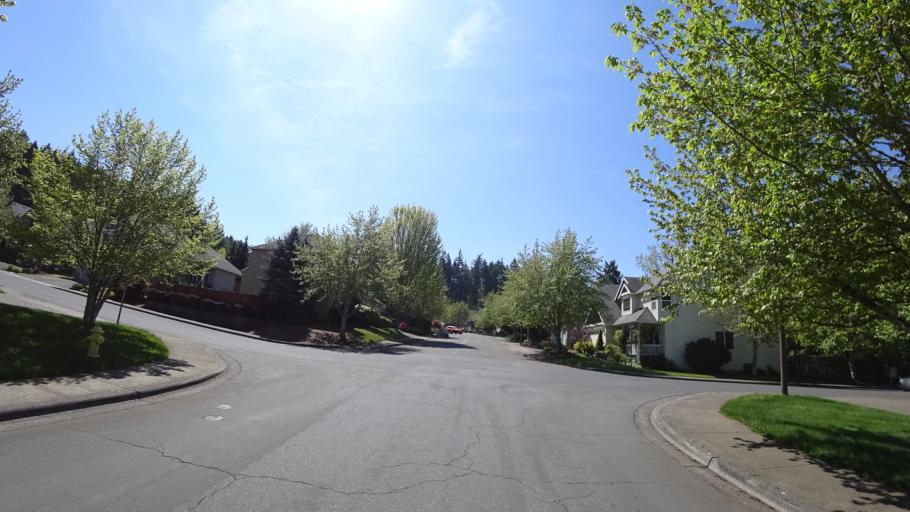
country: US
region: Oregon
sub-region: Washington County
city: King City
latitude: 45.4278
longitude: -122.8272
